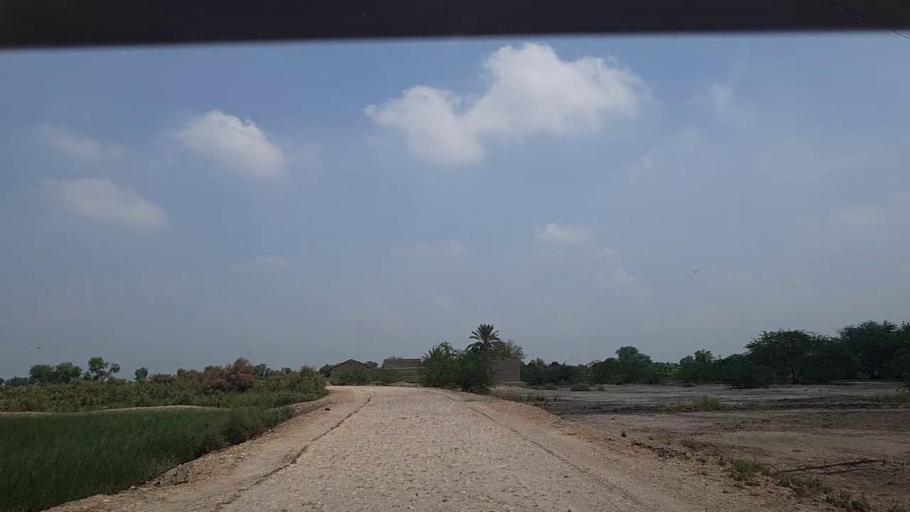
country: PK
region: Sindh
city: Khanpur
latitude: 27.8926
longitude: 69.4004
